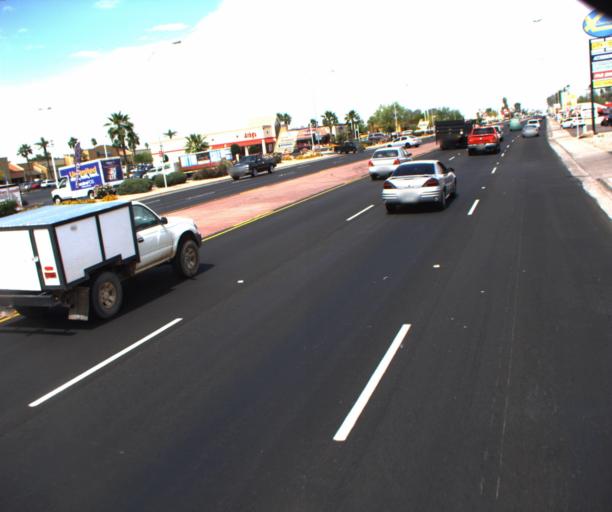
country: US
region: Arizona
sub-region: Maricopa County
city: Mesa
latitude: 33.3947
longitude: -111.8399
